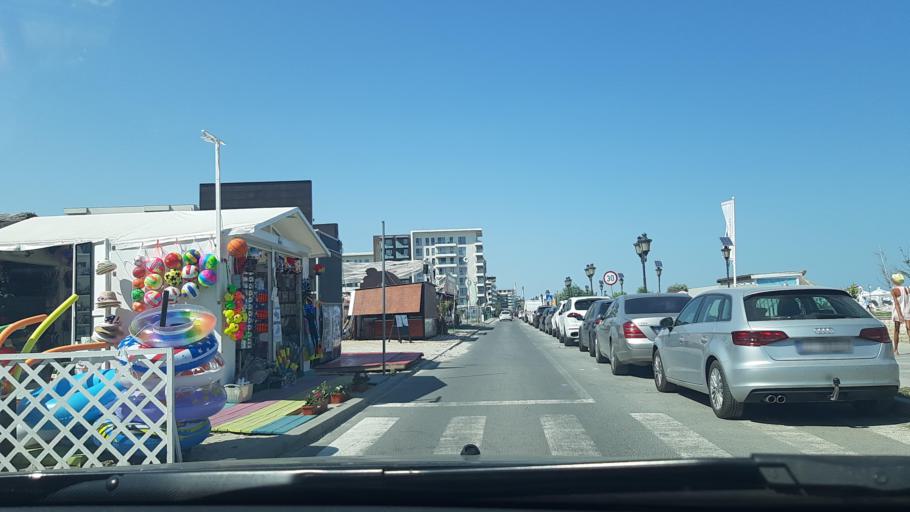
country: RO
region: Constanta
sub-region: Comuna Navodari
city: Navodari
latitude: 44.3028
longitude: 28.6270
